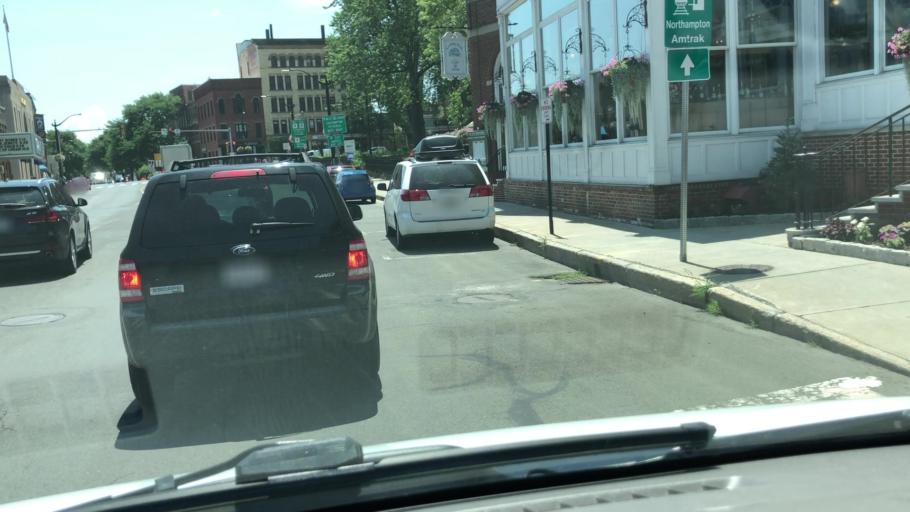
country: US
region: Massachusetts
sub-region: Hampshire County
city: Northampton
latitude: 42.3203
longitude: -72.6306
